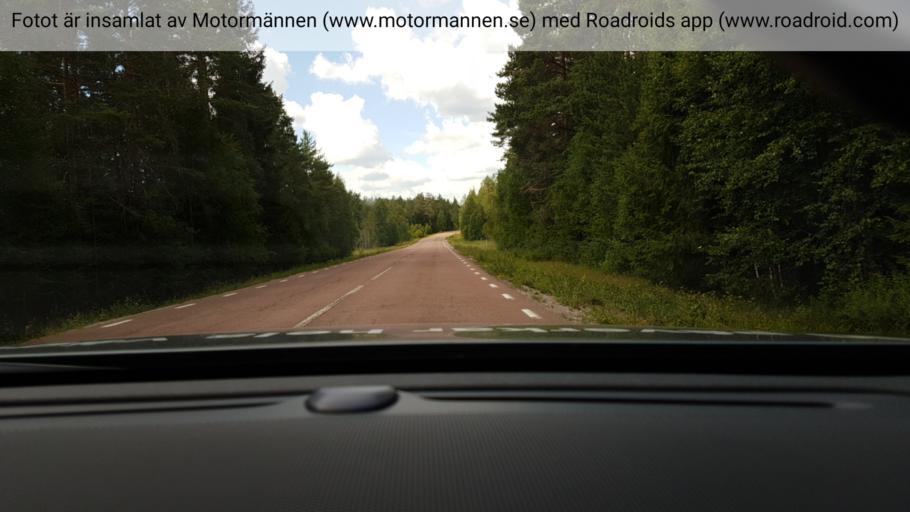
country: SE
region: Dalarna
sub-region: Rattviks Kommun
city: Raettvik
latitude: 61.0061
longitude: 15.3375
